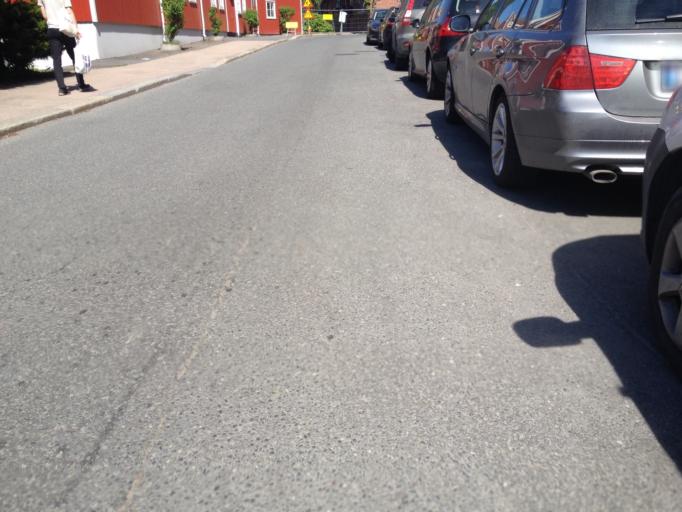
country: NO
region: Oslo
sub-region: Oslo
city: Oslo
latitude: 59.9348
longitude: 10.7623
